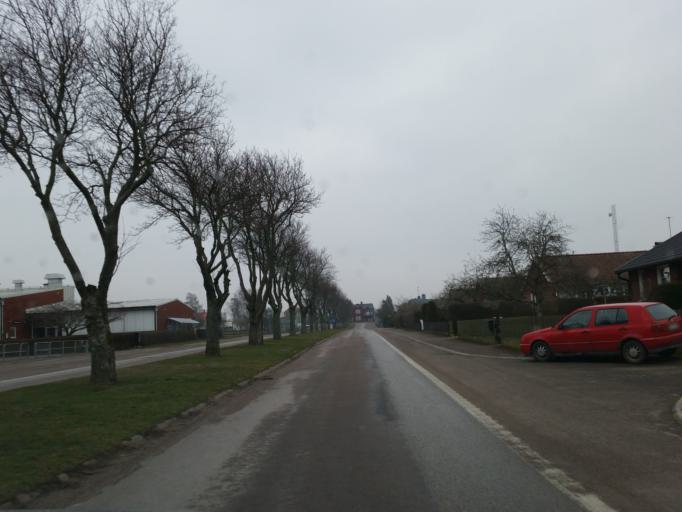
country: SE
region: Kalmar
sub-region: Morbylanga Kommun
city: Moerbylanga
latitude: 56.5231
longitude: 16.3838
